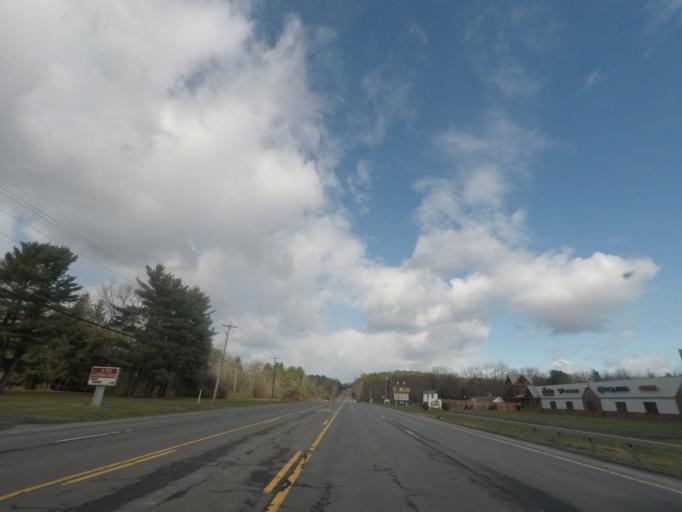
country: US
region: New York
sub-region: Saratoga County
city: Ballston Spa
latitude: 43.0030
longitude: -73.7905
